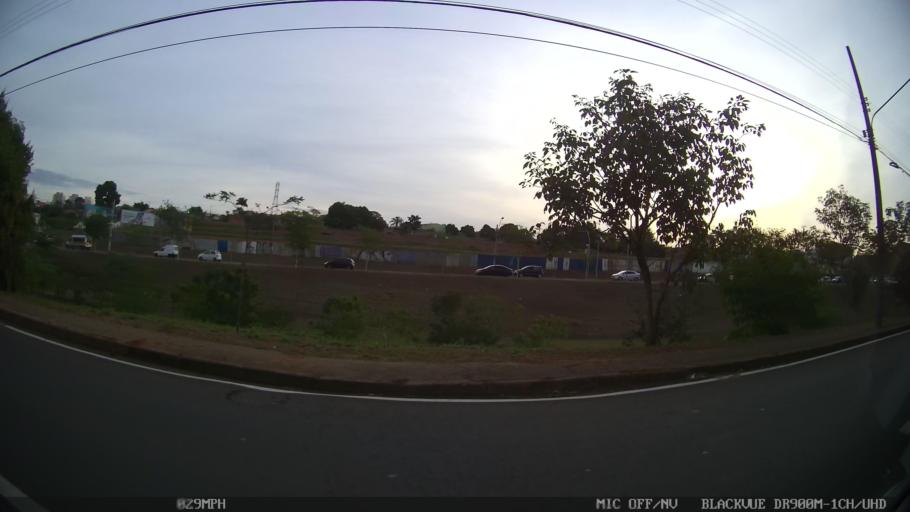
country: BR
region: Sao Paulo
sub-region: Limeira
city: Limeira
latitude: -22.5690
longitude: -47.4154
